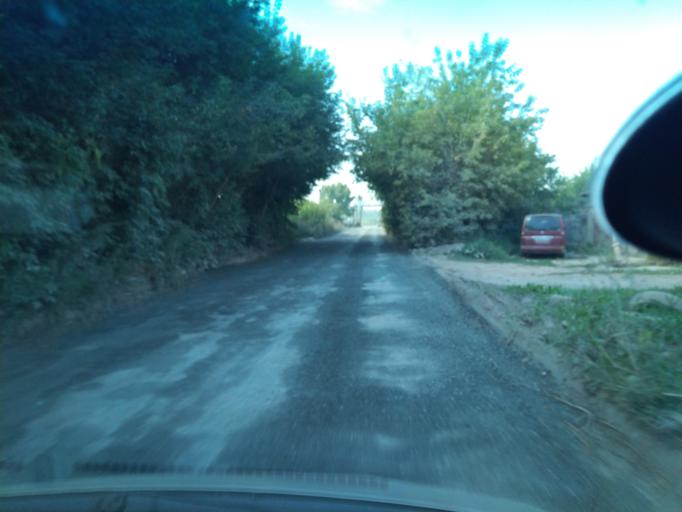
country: RU
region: Krasnoyarskiy
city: Krasnoyarsk
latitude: 55.9744
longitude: 92.9440
